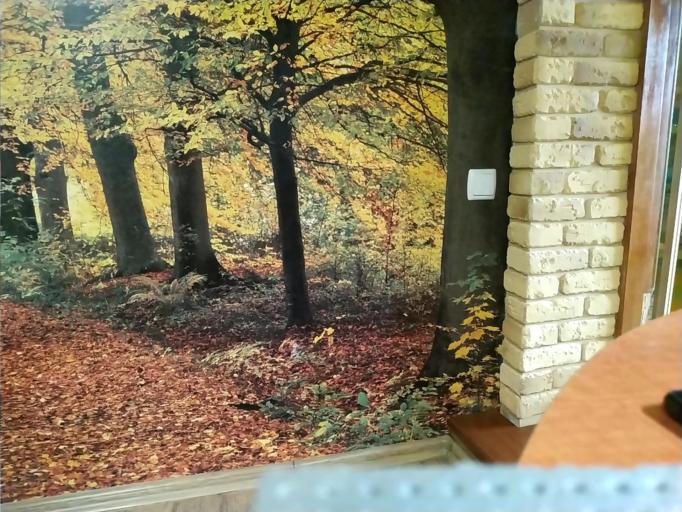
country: RU
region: Vladimir
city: Bavleny
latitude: 56.3663
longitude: 39.5455
